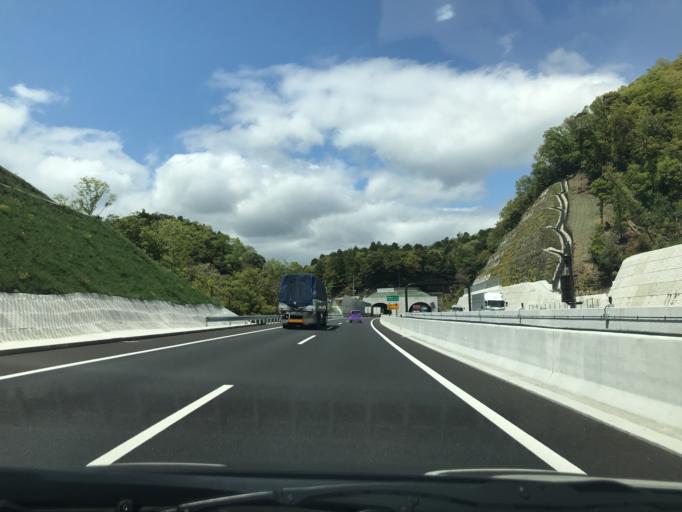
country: JP
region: Osaka
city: Takatsuki
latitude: 34.8920
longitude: 135.6093
